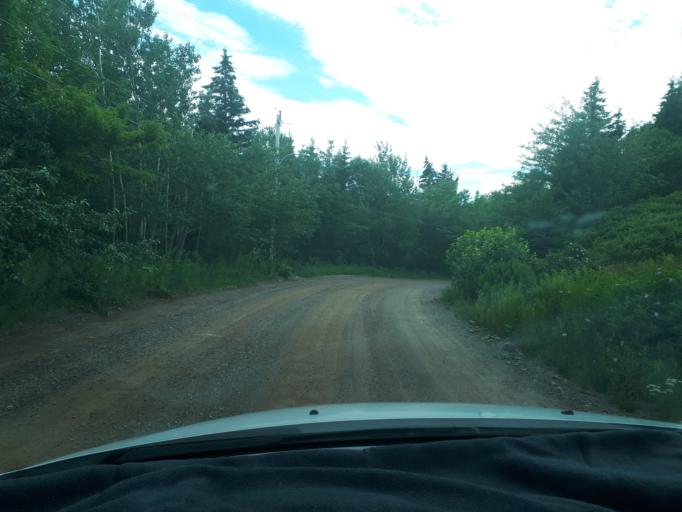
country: CA
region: Nova Scotia
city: Sydney Mines
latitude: 46.3287
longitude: -60.4195
